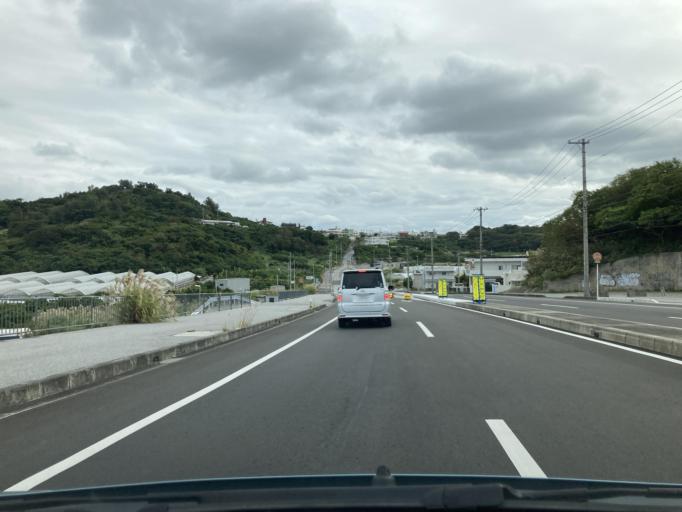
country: JP
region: Okinawa
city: Tomigusuku
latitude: 26.1674
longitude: 127.6776
